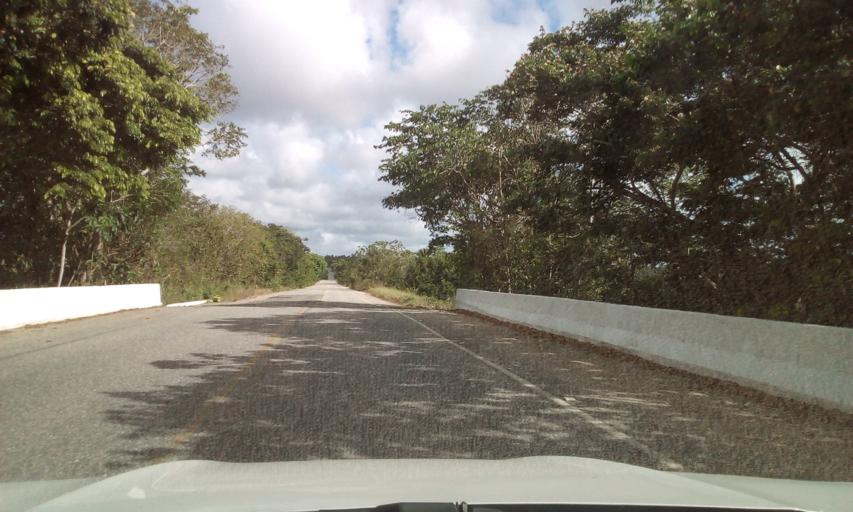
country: BR
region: Sergipe
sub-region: Indiaroba
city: Indiaroba
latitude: -11.4740
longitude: -37.4920
